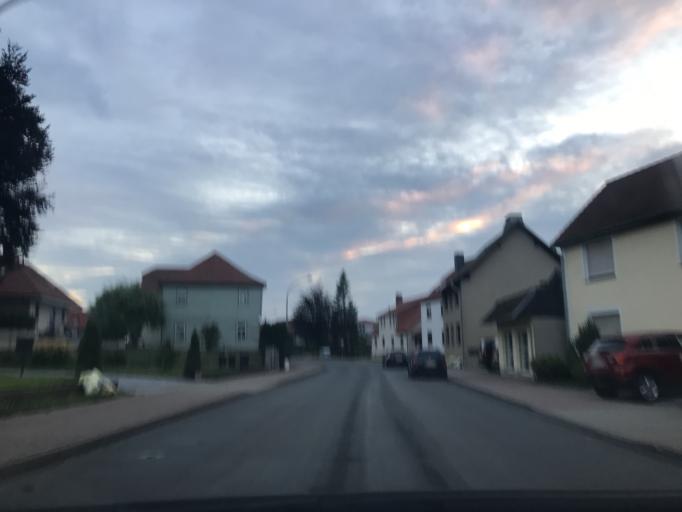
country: DE
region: Thuringia
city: Niederorschel
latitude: 51.3666
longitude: 10.4238
